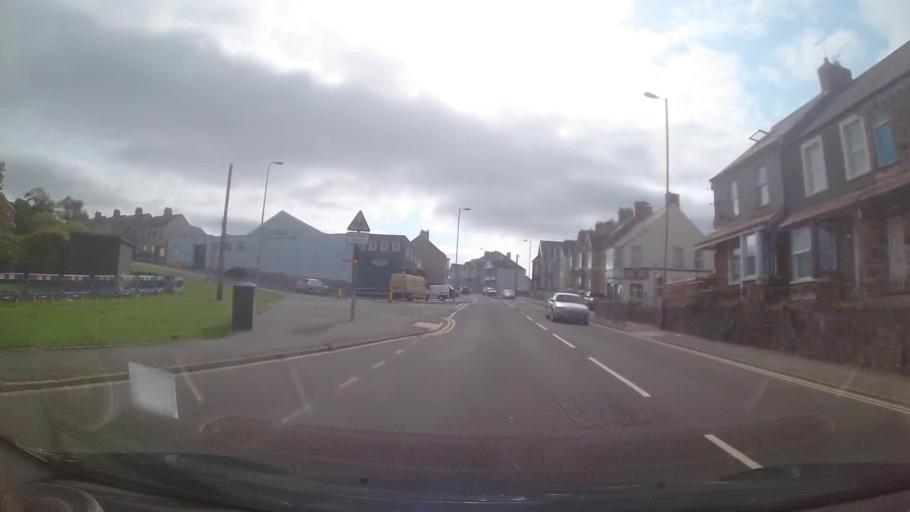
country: GB
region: Wales
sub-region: Pembrokeshire
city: Milford Haven
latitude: 51.7168
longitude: -5.0269
